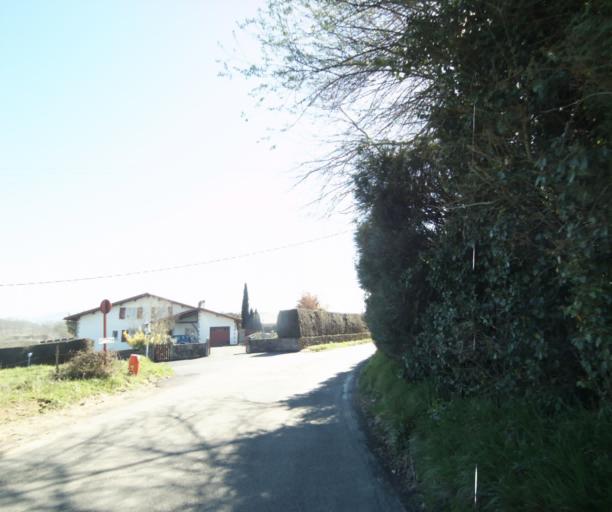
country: FR
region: Aquitaine
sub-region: Departement des Pyrenees-Atlantiques
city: Ciboure
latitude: 43.3745
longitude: -1.6875
